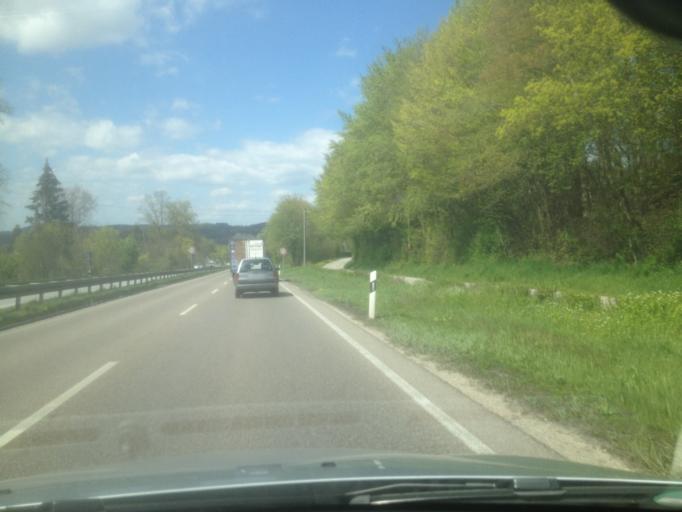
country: DE
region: Bavaria
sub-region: Swabia
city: Diedorf
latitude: 48.3706
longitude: 10.8093
